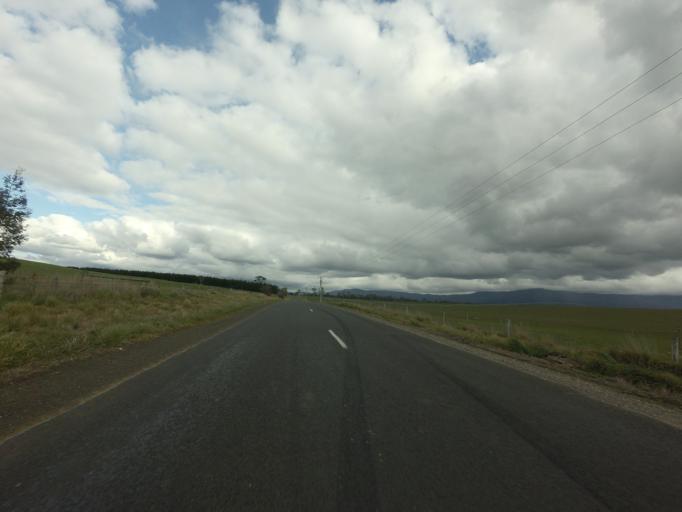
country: AU
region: Tasmania
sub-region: Northern Midlands
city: Longford
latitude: -41.7558
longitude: 147.0825
